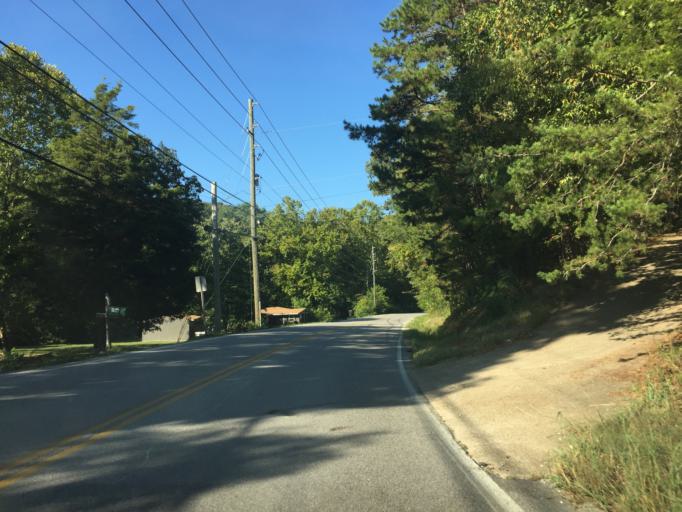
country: US
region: Tennessee
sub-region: Hamilton County
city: Harrison
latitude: 35.1187
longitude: -85.1127
